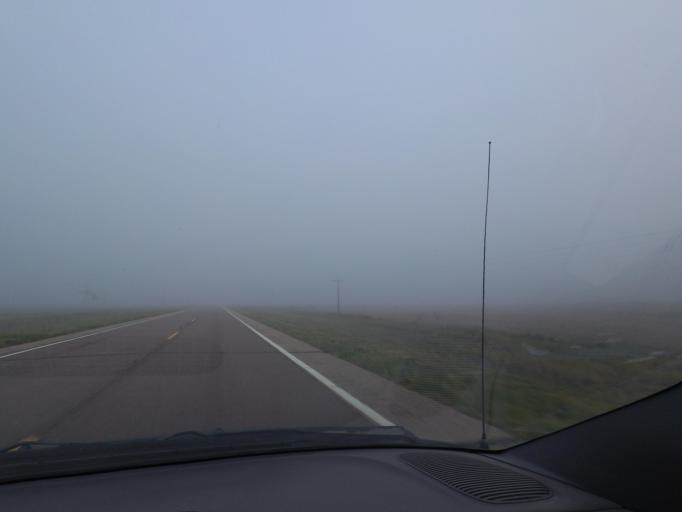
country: US
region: Colorado
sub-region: Kit Carson County
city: Burlington
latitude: 39.6581
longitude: -102.5252
